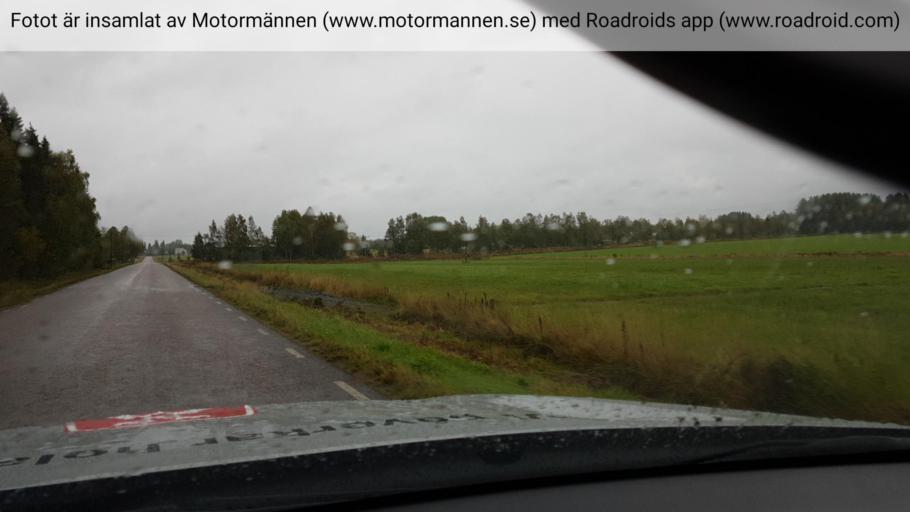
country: SE
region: Norrbotten
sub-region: Lulea Kommun
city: Gammelstad
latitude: 65.7532
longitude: 22.1019
